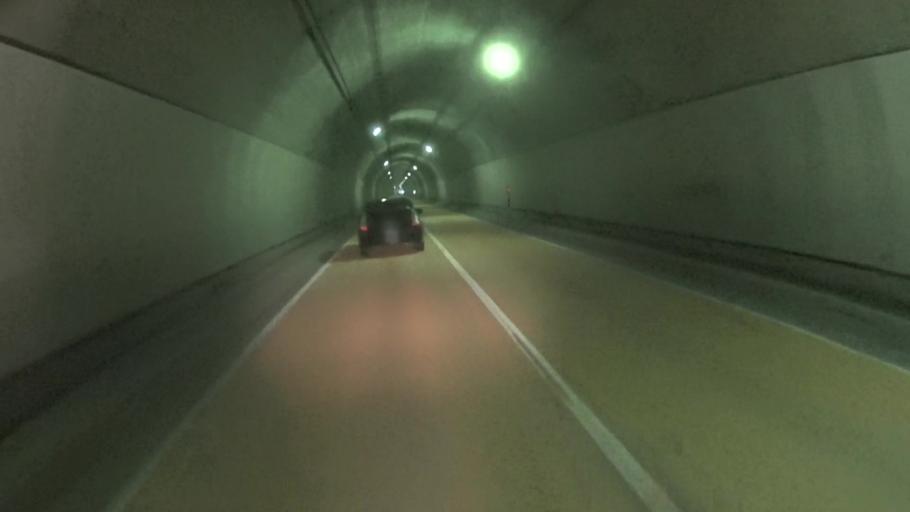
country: JP
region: Kyoto
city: Ayabe
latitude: 35.2719
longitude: 135.2672
